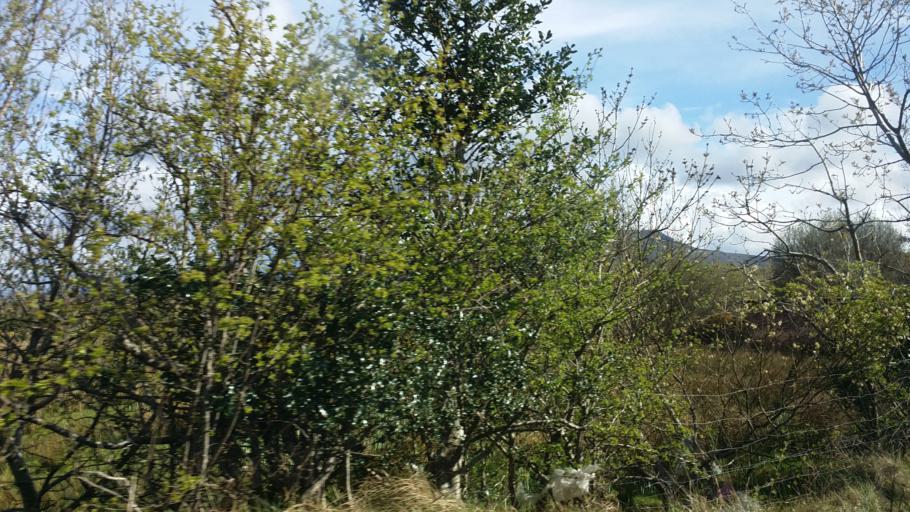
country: IE
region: Ulster
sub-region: County Donegal
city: Bundoran
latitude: 54.4653
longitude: -8.2813
